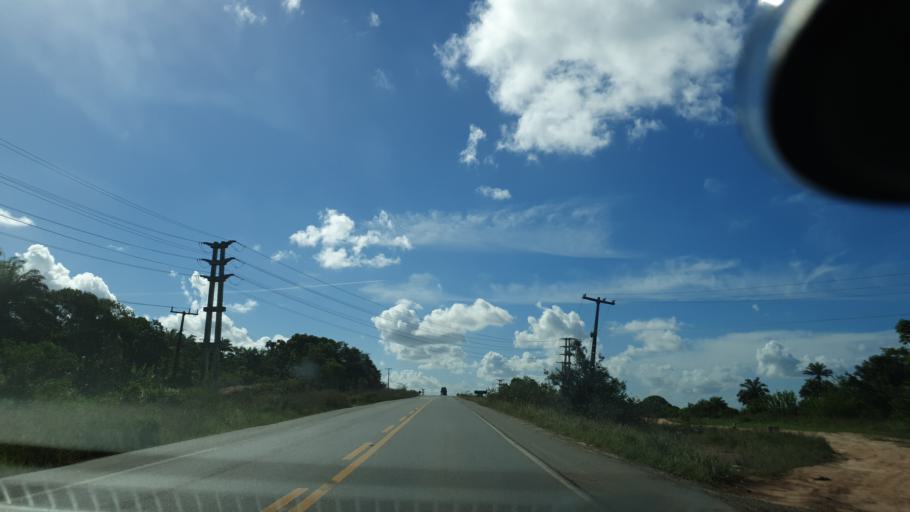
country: BR
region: Bahia
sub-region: Camacari
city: Camacari
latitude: -12.6825
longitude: -38.2379
